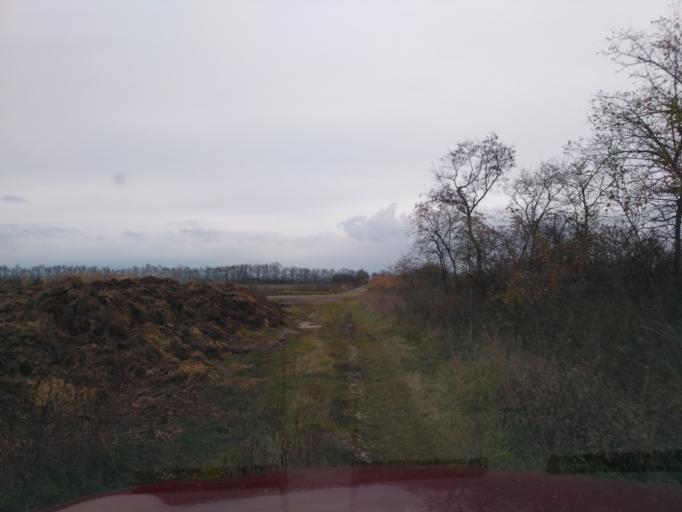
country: HU
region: Borsod-Abauj-Zemplen
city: Gonc
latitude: 48.5662
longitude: 21.1572
